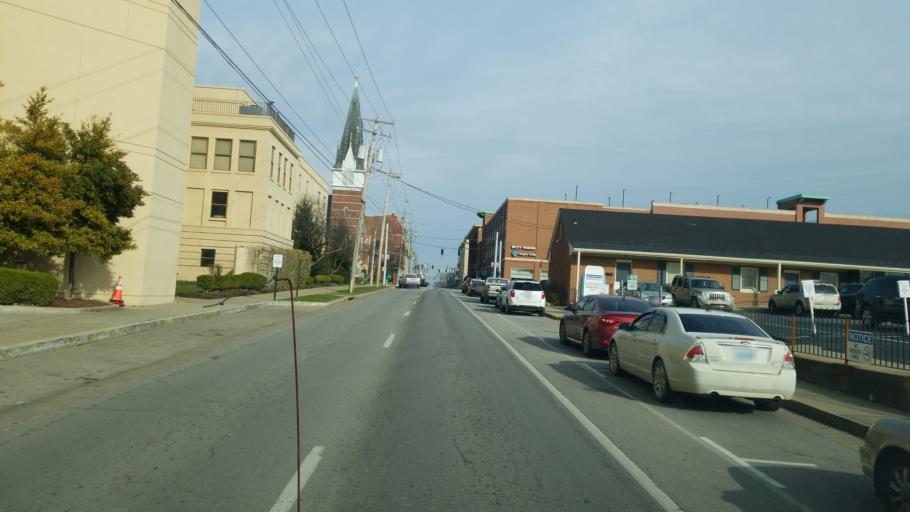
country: US
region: Kentucky
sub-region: Boyle County
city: Danville
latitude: 37.6439
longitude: -84.7727
